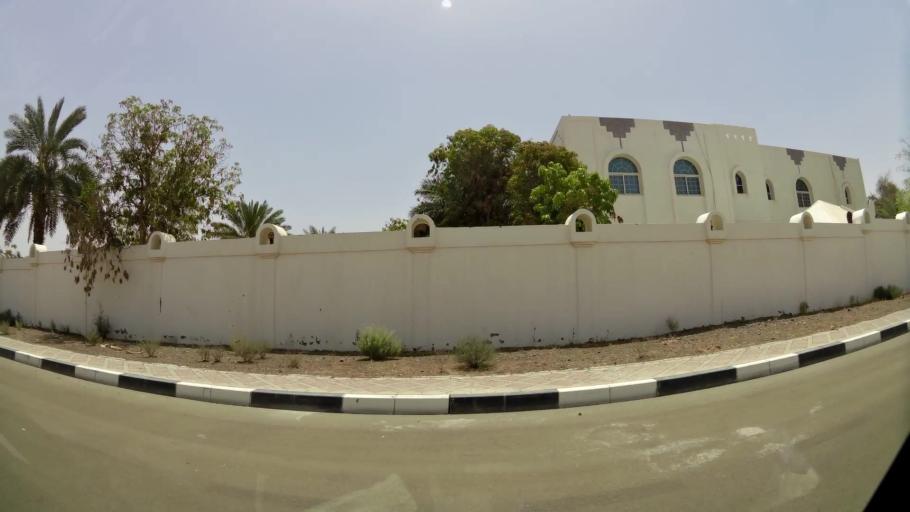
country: AE
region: Abu Dhabi
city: Al Ain
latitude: 24.1978
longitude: 55.7380
